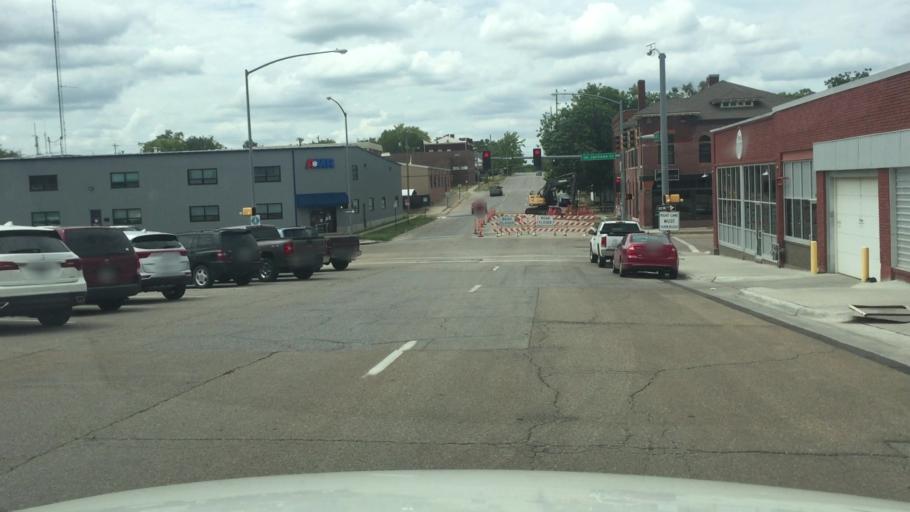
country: US
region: Kansas
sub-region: Shawnee County
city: Topeka
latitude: 39.0548
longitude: -95.6729
